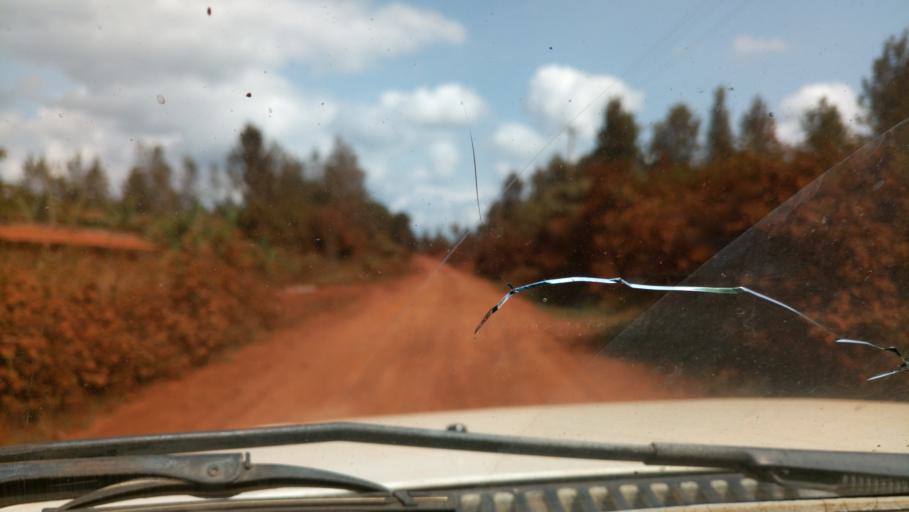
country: KE
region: Murang'a District
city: Karuri
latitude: -0.7556
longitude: 37.2117
